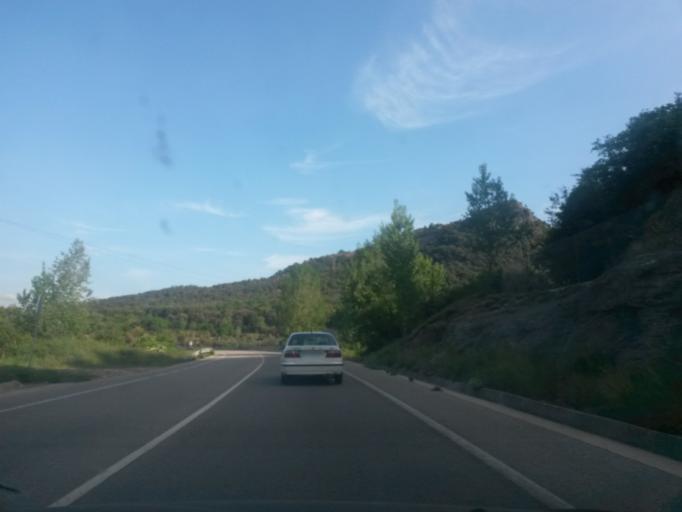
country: ES
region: Catalonia
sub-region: Provincia de Girona
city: les Planes d'Hostoles
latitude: 42.0644
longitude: 2.5314
